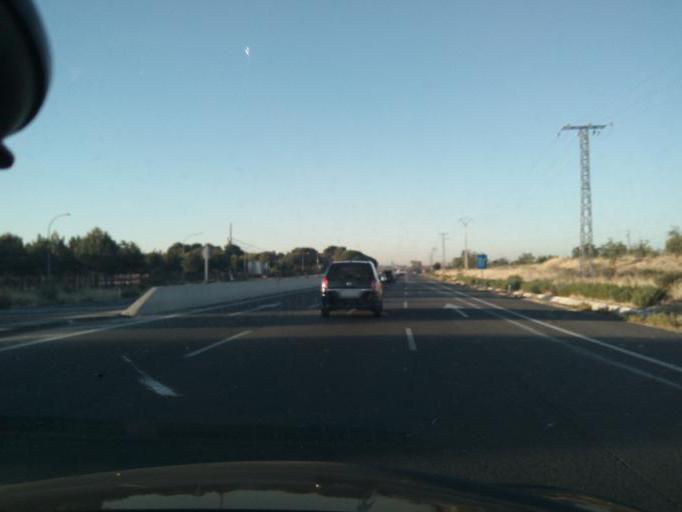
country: ES
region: Madrid
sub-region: Provincia de Madrid
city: Torrejon de Ardoz
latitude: 40.4917
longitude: -3.4787
